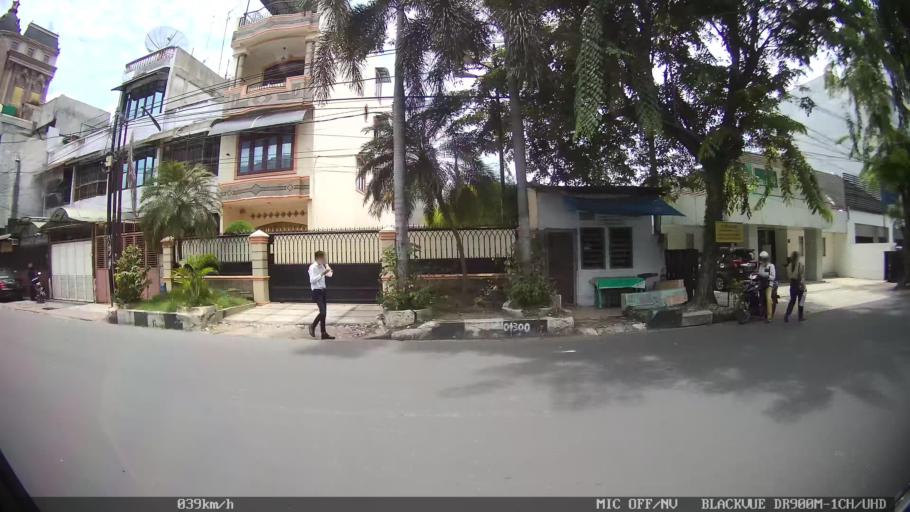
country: ID
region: North Sumatra
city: Medan
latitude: 3.5867
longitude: 98.6674
